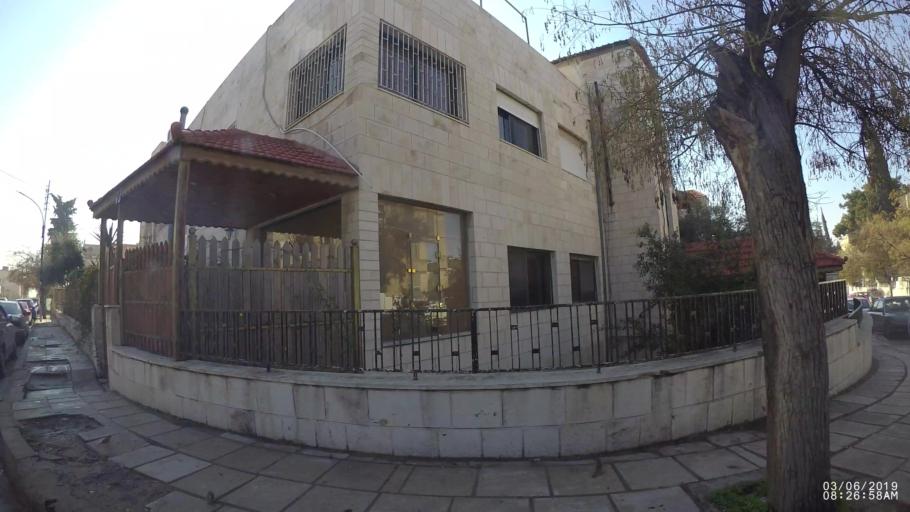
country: JO
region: Amman
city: Amman
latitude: 31.9841
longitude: 35.9895
